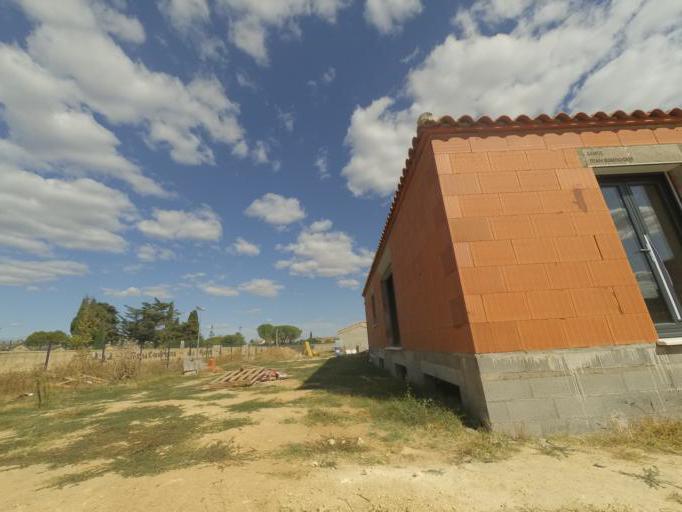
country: FR
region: Languedoc-Roussillon
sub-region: Departement du Gard
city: Codognan
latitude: 43.7340
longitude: 4.2218
